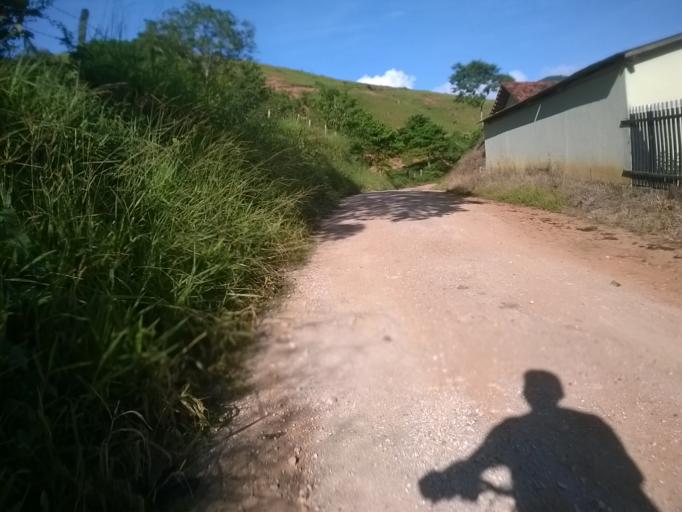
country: BR
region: Minas Gerais
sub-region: Uba
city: Uba
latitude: -21.0885
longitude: -43.0076
